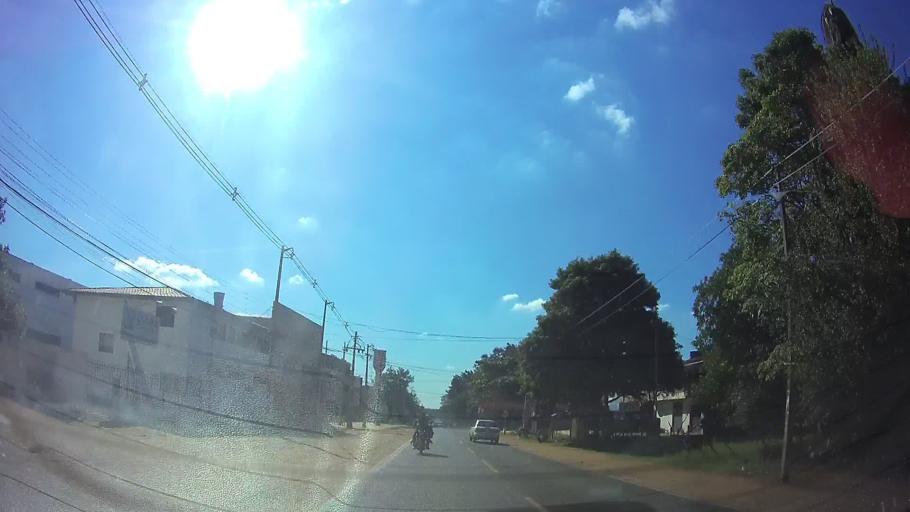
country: PY
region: Central
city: Limpio
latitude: -25.2342
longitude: -57.4753
